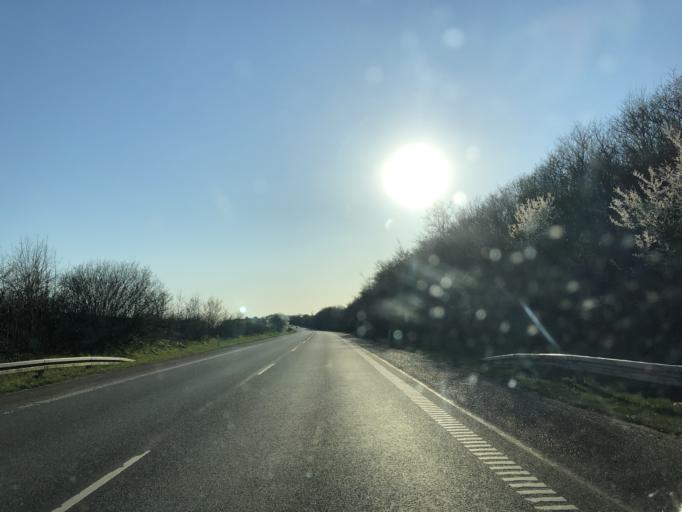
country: DK
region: North Denmark
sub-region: Vesthimmerland Kommune
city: Aars
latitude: 56.8179
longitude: 9.6803
